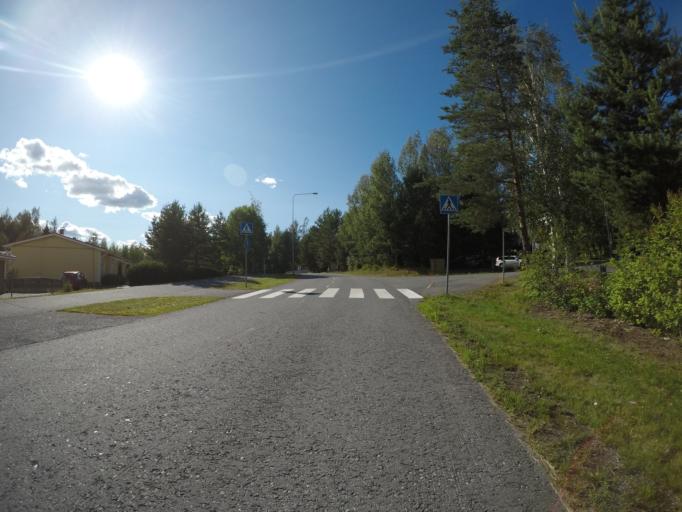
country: FI
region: Haeme
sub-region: Haemeenlinna
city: Haemeenlinna
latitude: 61.0220
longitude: 24.5183
